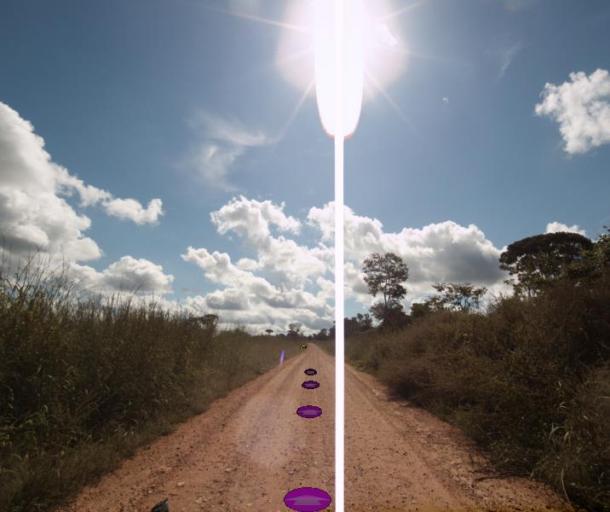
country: BR
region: Goias
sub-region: Jaragua
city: Jaragua
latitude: -15.8194
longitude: -49.1848
